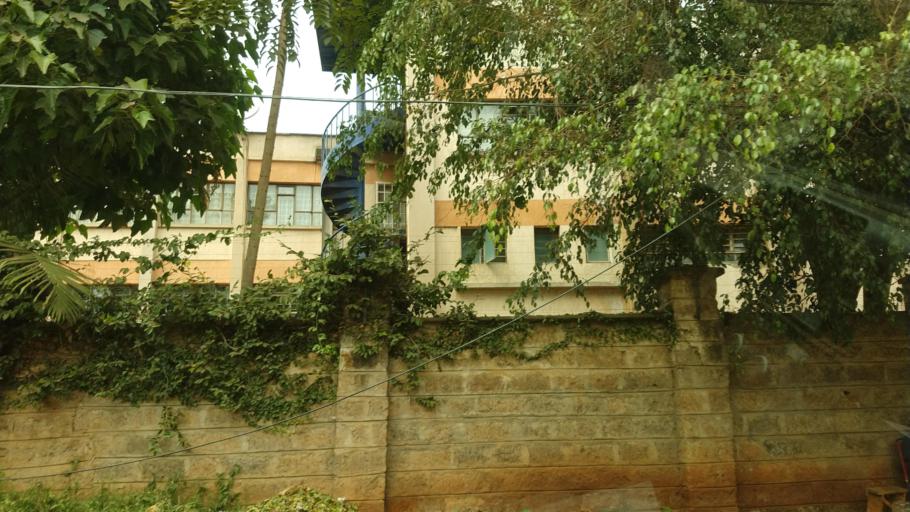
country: KE
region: Nairobi Area
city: Nairobi
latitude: -1.2993
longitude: 36.7769
